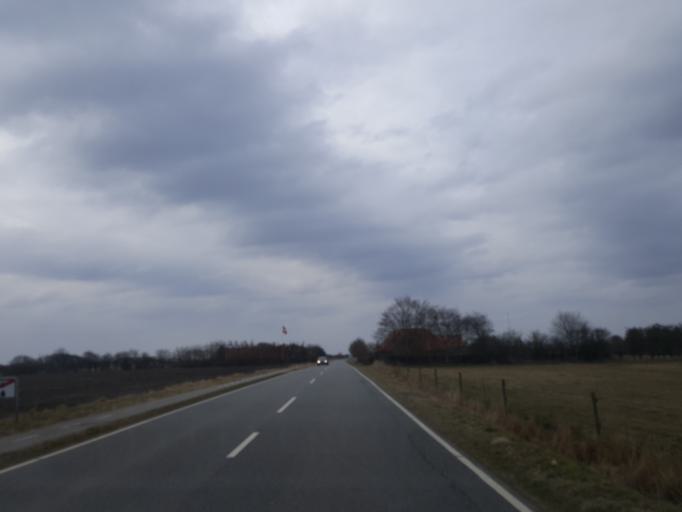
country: DK
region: Central Jutland
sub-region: Holstebro Kommune
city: Ulfborg
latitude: 56.3418
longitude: 8.3330
